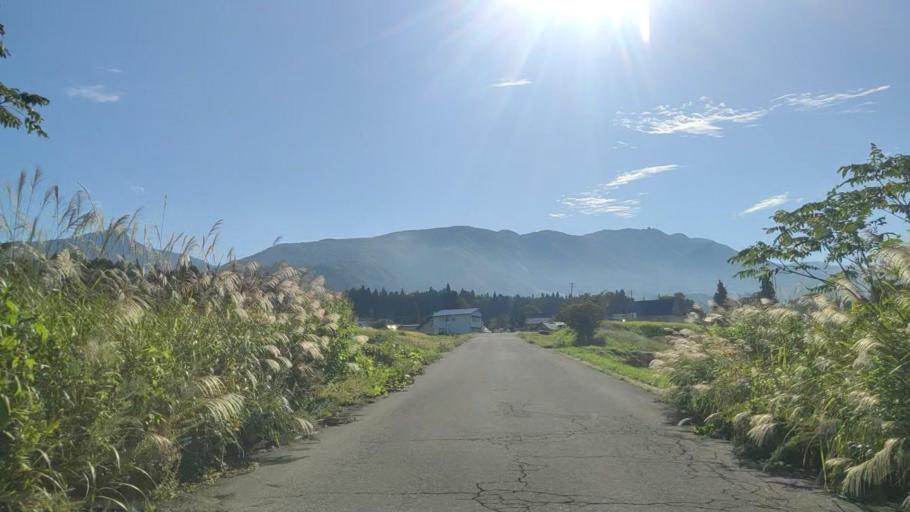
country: JP
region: Nagano
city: Iiyama
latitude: 36.8044
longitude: 138.4303
